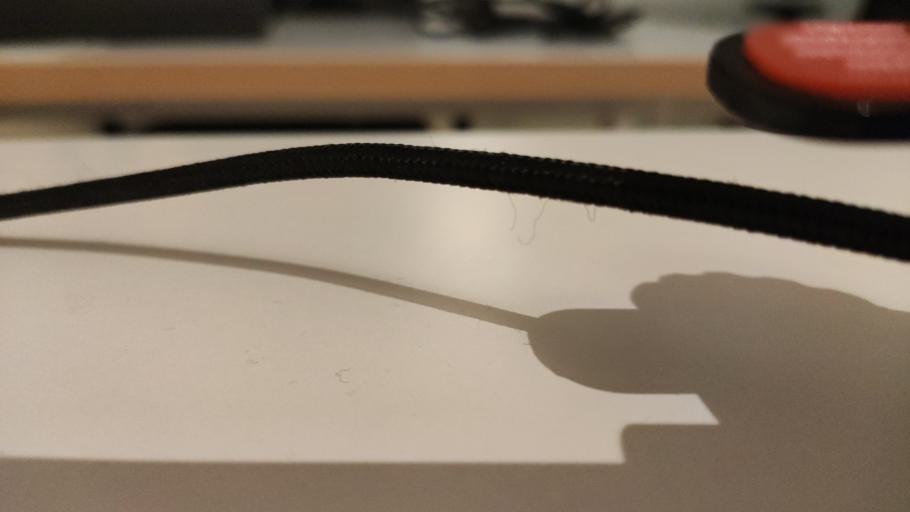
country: RU
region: Moskovskaya
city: Shaburnovo
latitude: 56.4202
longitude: 37.9797
